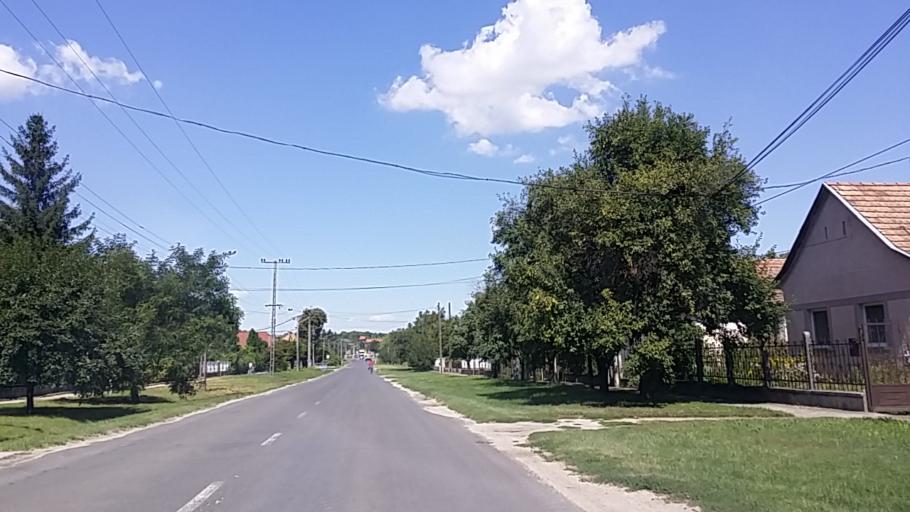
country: HU
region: Tolna
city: Simontornya
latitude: 46.7539
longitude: 18.5458
